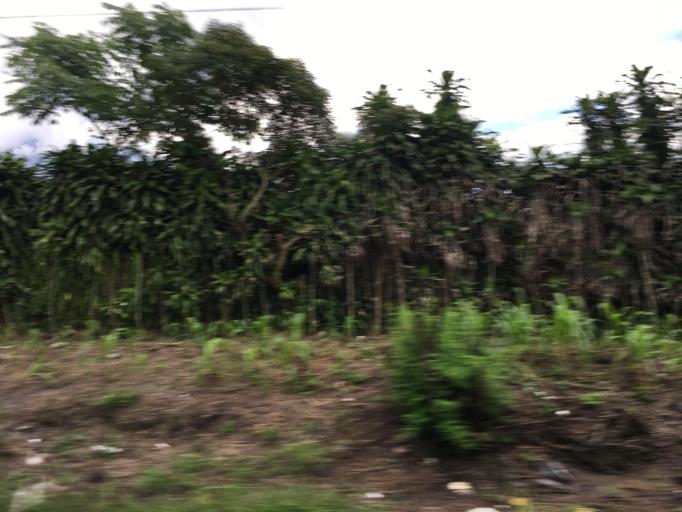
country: GT
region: Sacatepequez
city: Alotenango
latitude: 14.4009
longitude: -90.8279
